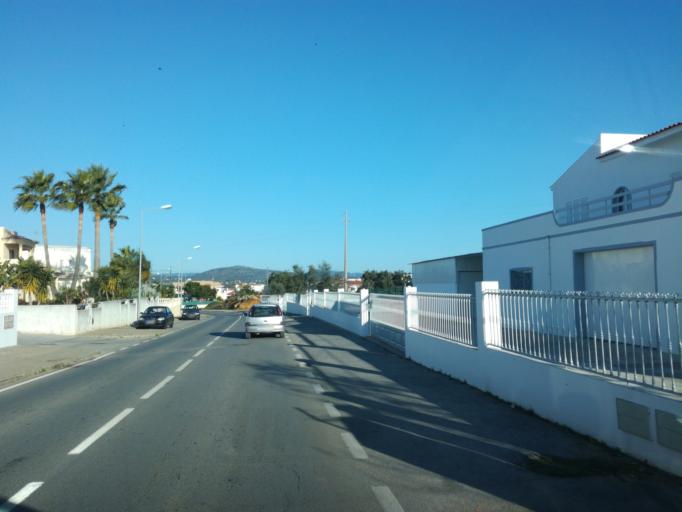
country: PT
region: Faro
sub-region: Olhao
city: Laranjeiro
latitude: 37.0587
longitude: -7.7626
